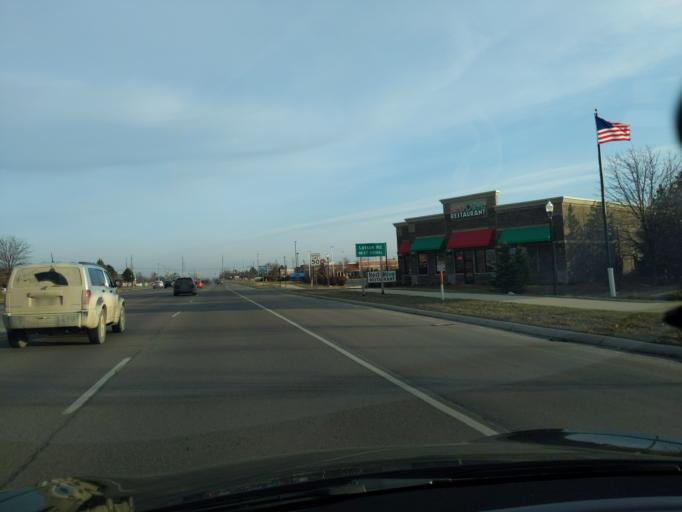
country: US
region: Michigan
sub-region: Livingston County
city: Howell
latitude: 42.5882
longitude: -83.8781
